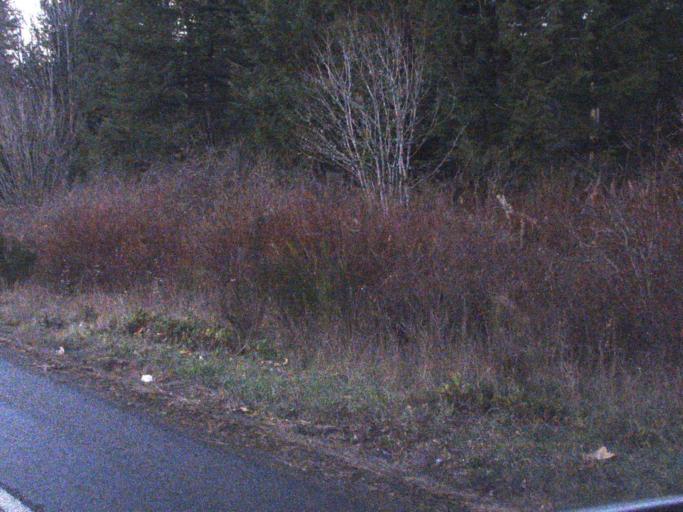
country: US
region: Washington
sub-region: Skagit County
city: Sedro-Woolley
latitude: 48.5280
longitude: -121.9172
